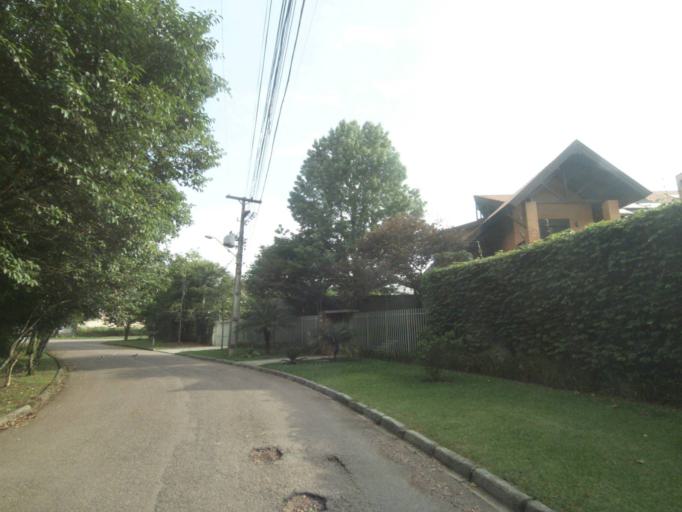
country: BR
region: Parana
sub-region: Curitiba
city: Curitiba
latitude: -25.4166
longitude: -49.3106
